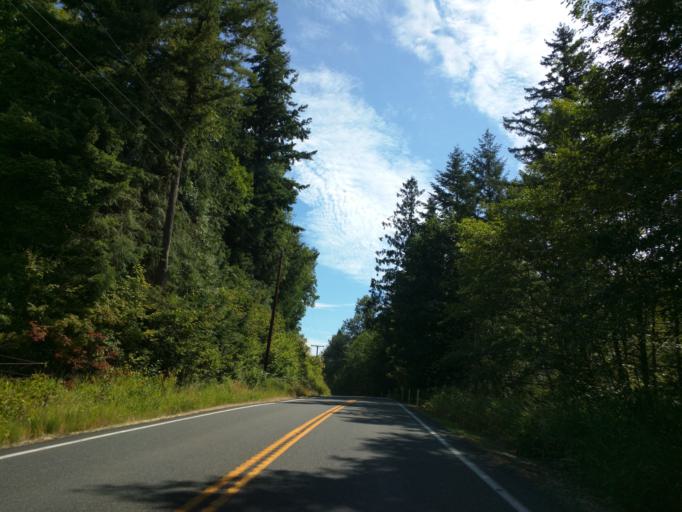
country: US
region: Washington
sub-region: Whatcom County
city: Sumas
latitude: 48.9664
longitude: -122.2174
